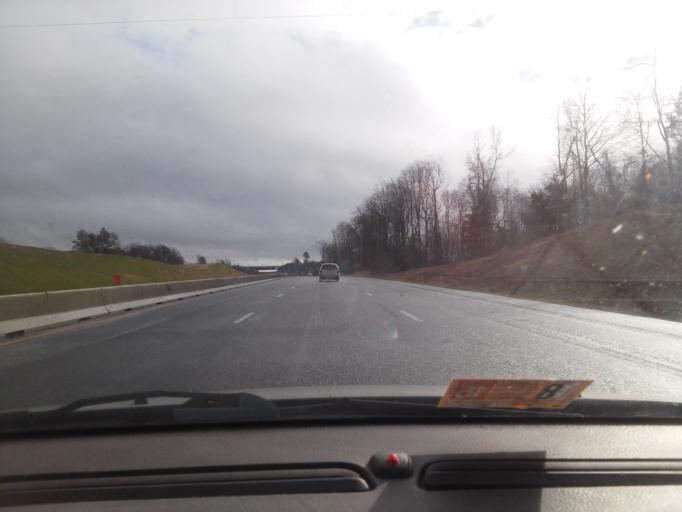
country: US
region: Virginia
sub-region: Henrico County
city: Short Pump
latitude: 37.6646
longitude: -77.6361
